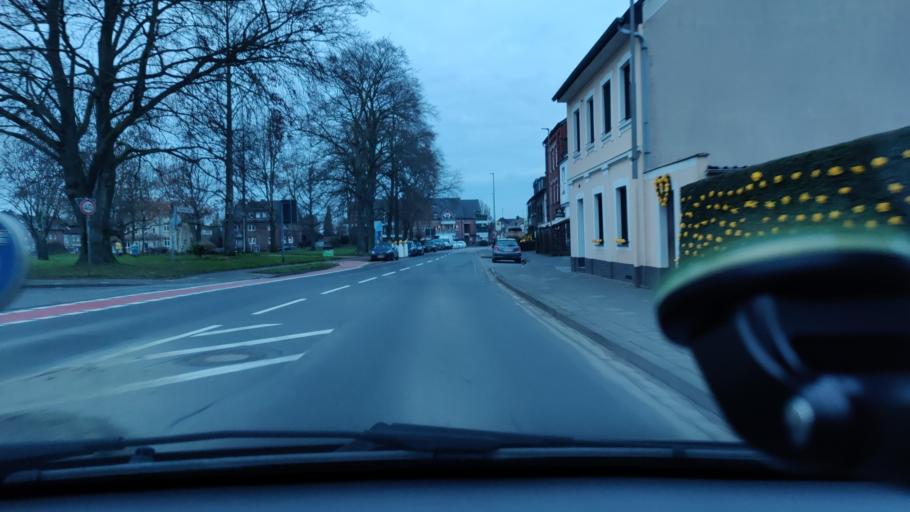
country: DE
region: North Rhine-Westphalia
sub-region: Regierungsbezirk Dusseldorf
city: Viersen
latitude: 51.2893
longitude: 6.3668
